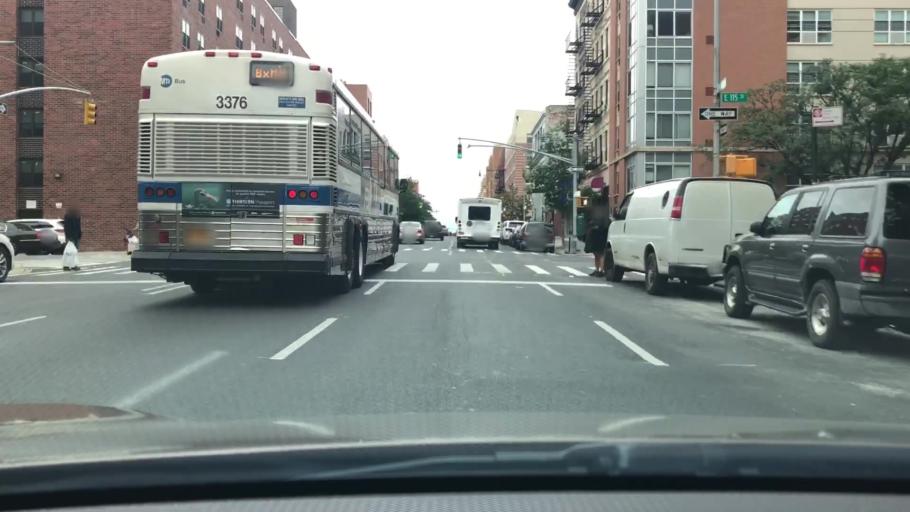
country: US
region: New York
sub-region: New York County
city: Manhattan
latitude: 40.7990
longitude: -73.9455
